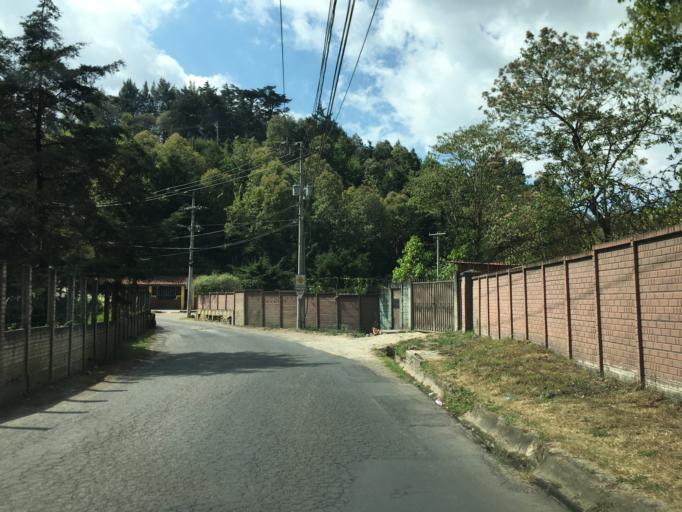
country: GT
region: Guatemala
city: San Jose Pinula
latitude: 14.5557
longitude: -90.4523
